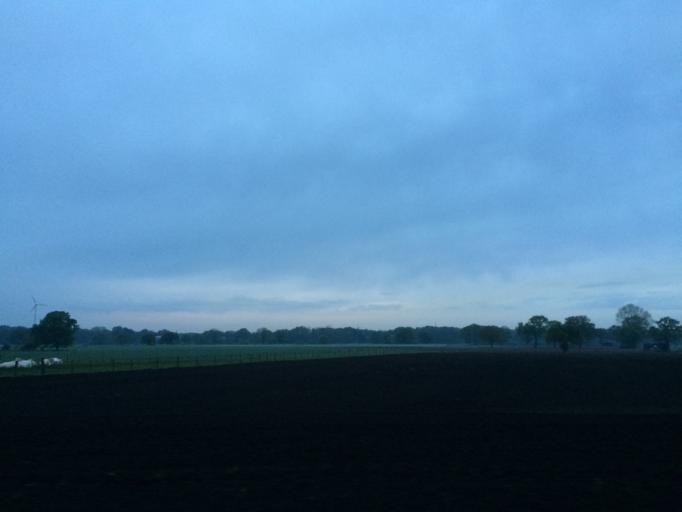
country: DE
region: North Rhine-Westphalia
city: Marl
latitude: 51.6821
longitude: 7.0526
